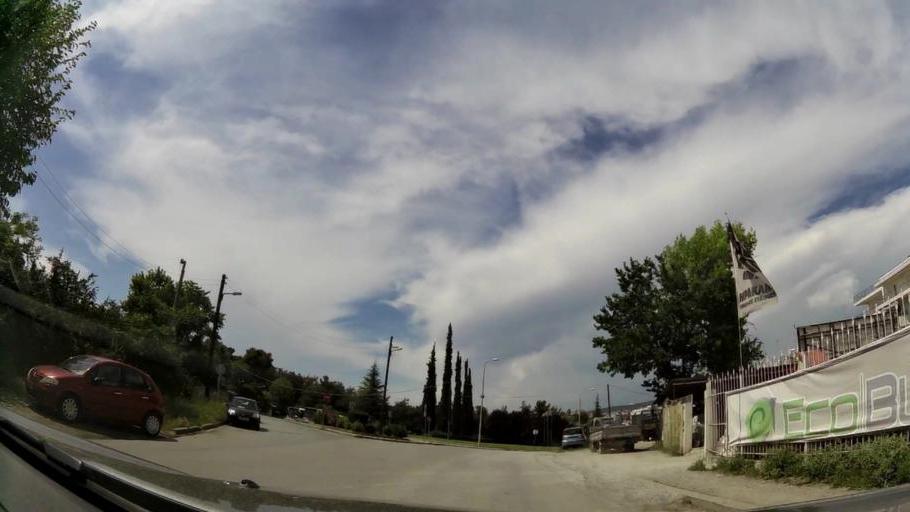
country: GR
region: Central Macedonia
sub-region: Nomos Thessalonikis
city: Pylaia
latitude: 40.5953
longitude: 22.9716
